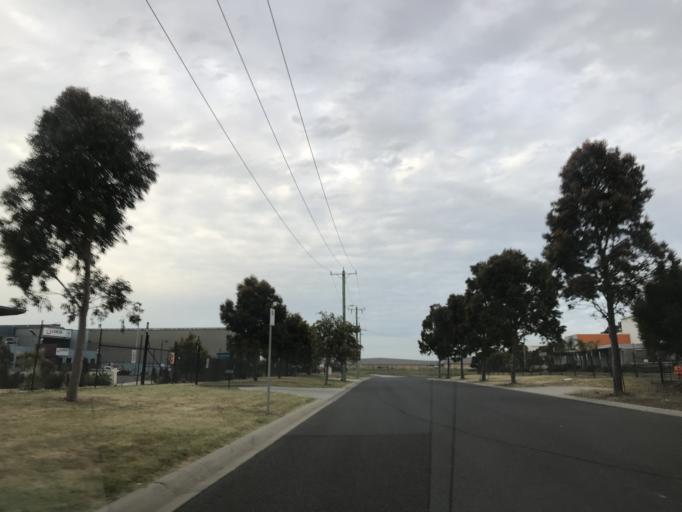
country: AU
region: Victoria
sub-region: Brimbank
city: Derrimut
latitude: -37.8100
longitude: 144.7748
